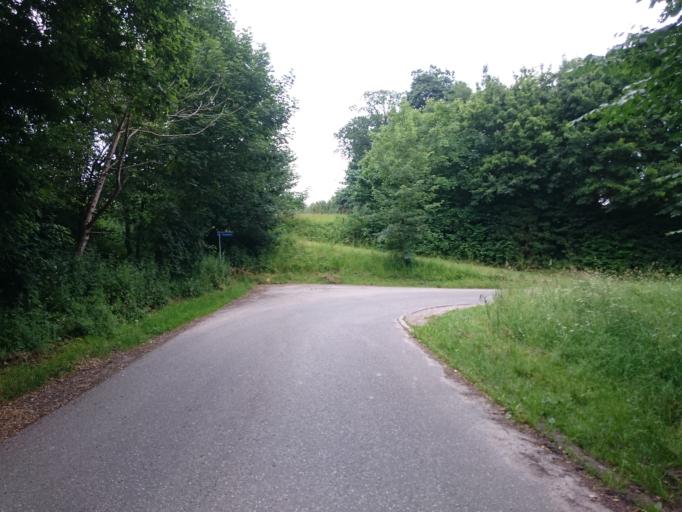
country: DK
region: South Denmark
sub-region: Nyborg Kommune
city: Nyborg
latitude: 55.3373
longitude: 10.7409
